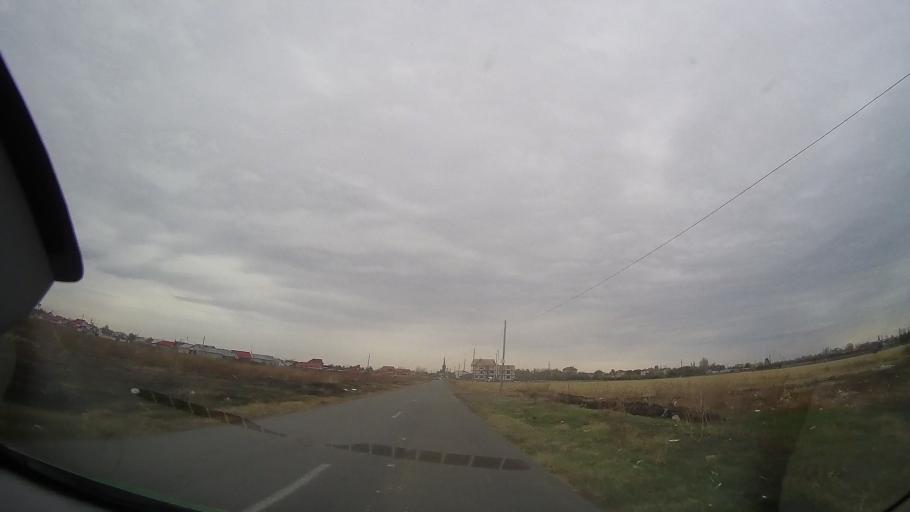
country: RO
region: Prahova
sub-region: Oras Mizil
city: Mizil
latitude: 45.0049
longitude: 26.4271
